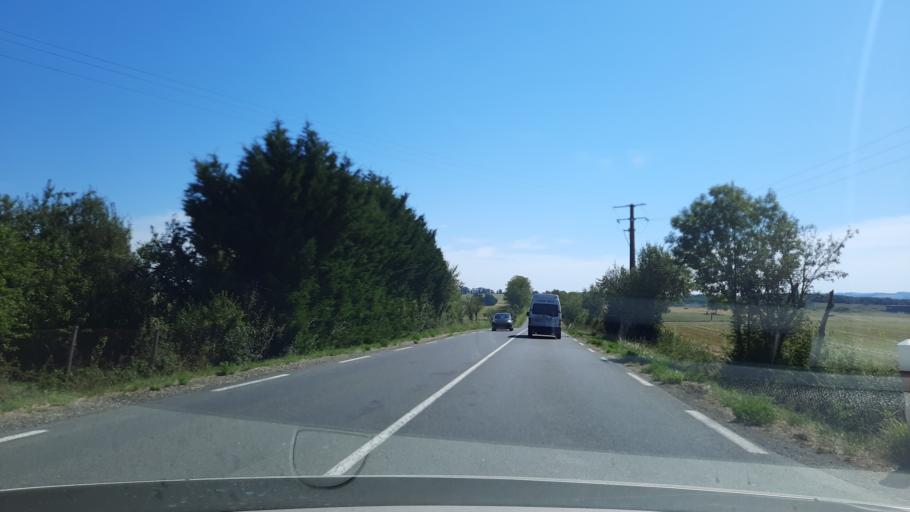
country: FR
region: Midi-Pyrenees
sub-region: Departement de l'Aveyron
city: Villefranche-de-Rouergue
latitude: 44.3463
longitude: 1.9586
